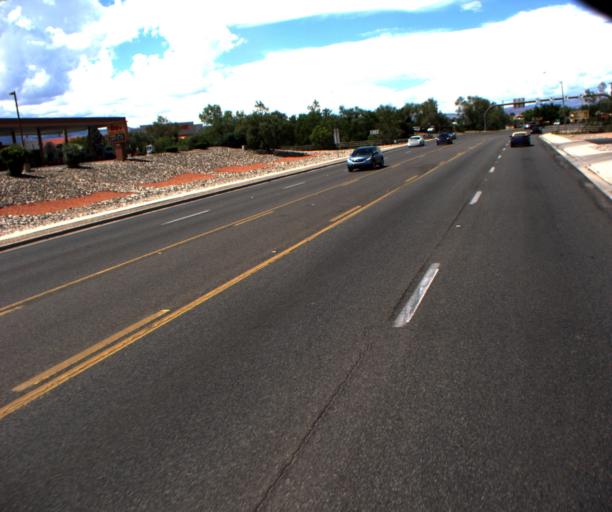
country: US
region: Arizona
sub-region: Yavapai County
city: Verde Village
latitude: 34.7194
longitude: -112.0019
